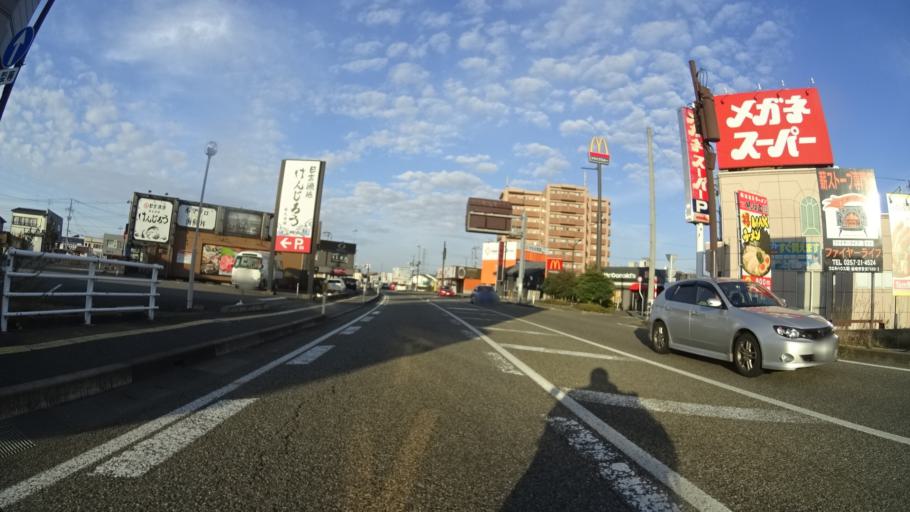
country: JP
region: Niigata
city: Kashiwazaki
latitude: 37.3691
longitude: 138.5772
